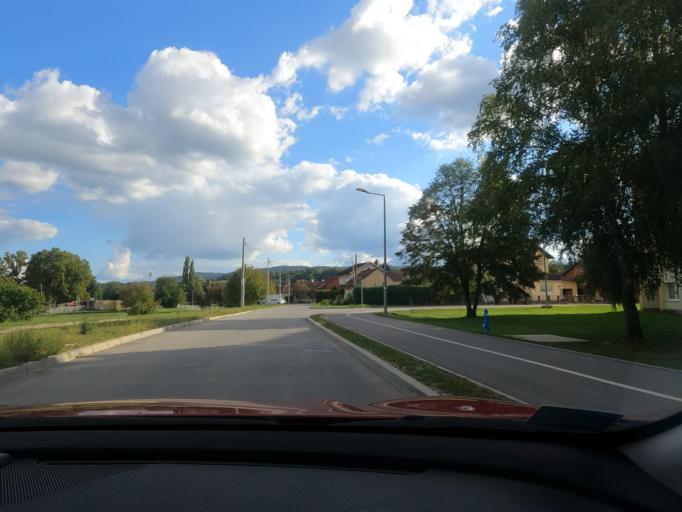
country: HR
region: Sisacko-Moslavacka
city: Petrinja
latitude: 45.4377
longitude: 16.2708
